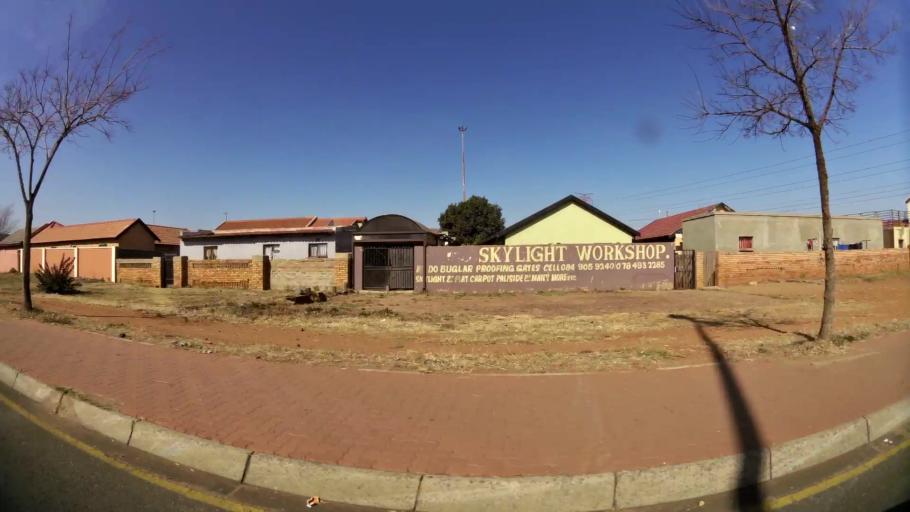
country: ZA
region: Gauteng
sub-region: City of Johannesburg Metropolitan Municipality
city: Soweto
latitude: -26.2857
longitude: 27.8523
